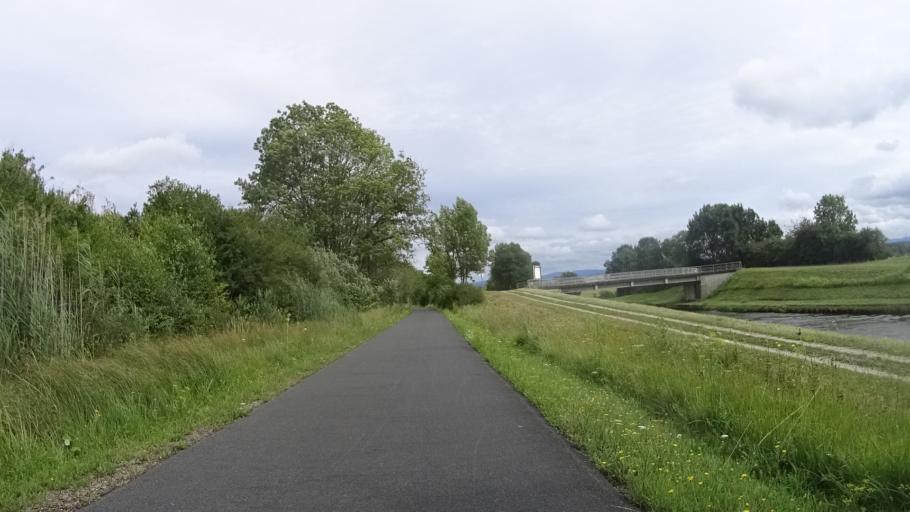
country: FR
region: Lorraine
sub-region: Departement de la Moselle
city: Sarrebourg
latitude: 48.6932
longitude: 7.0367
